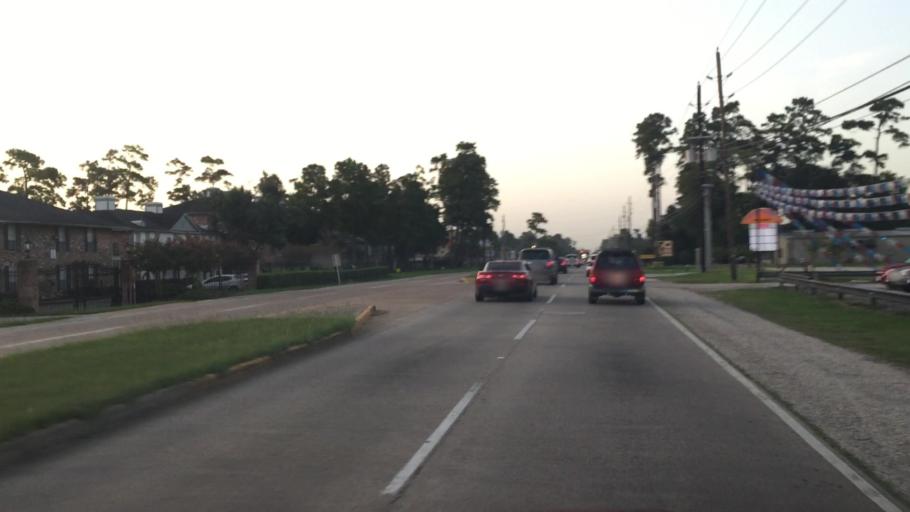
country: US
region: Texas
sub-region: Harris County
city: Hudson
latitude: 30.0153
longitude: -95.5183
